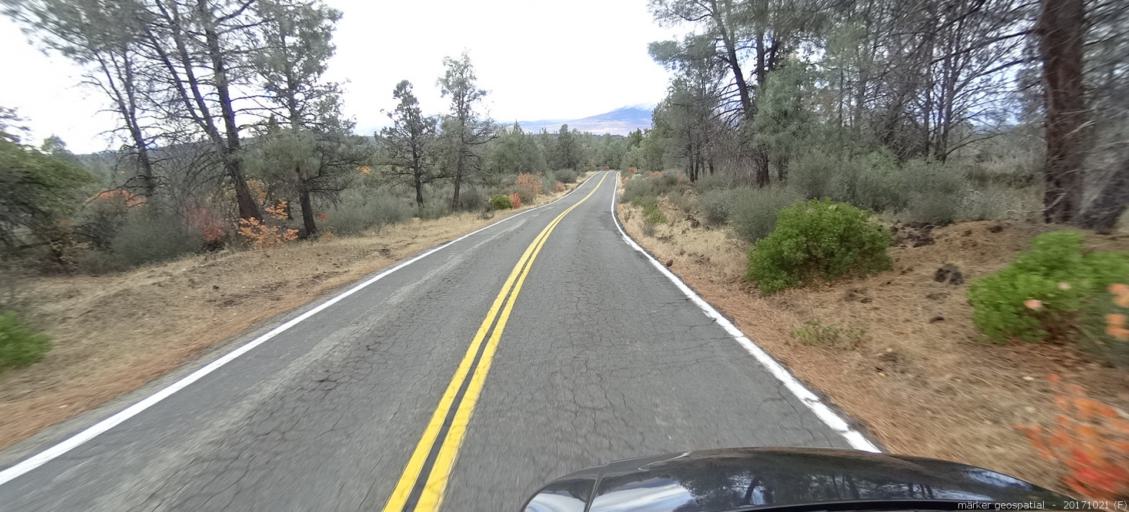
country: US
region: California
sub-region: Shasta County
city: Burney
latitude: 40.9203
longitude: -121.4820
